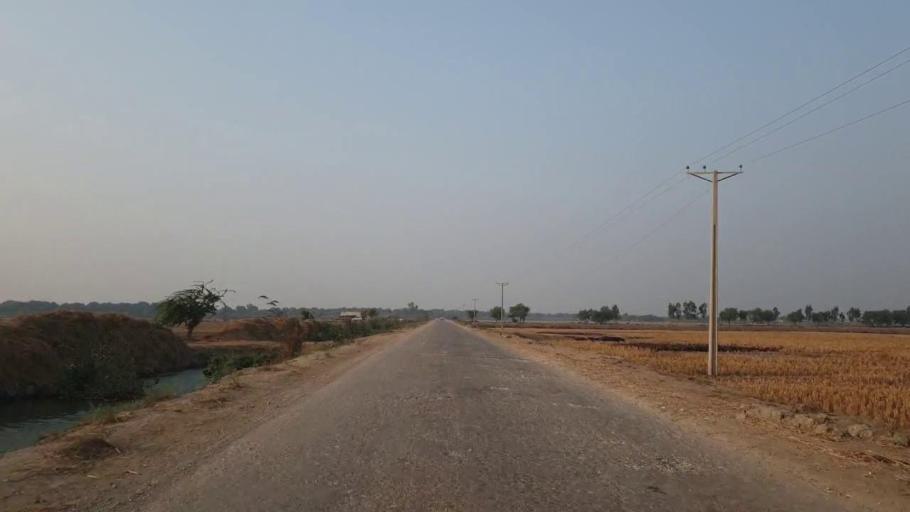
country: PK
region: Sindh
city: Tando Muhammad Khan
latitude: 25.1081
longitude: 68.4297
